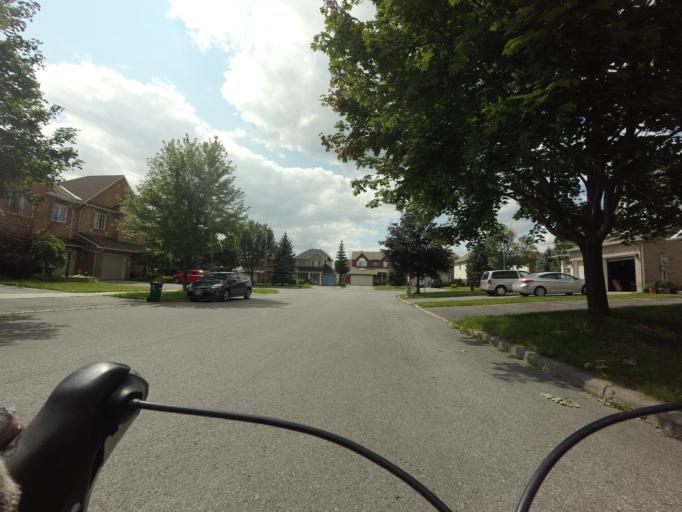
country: CA
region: Ontario
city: Bells Corners
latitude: 45.2799
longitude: -75.8459
